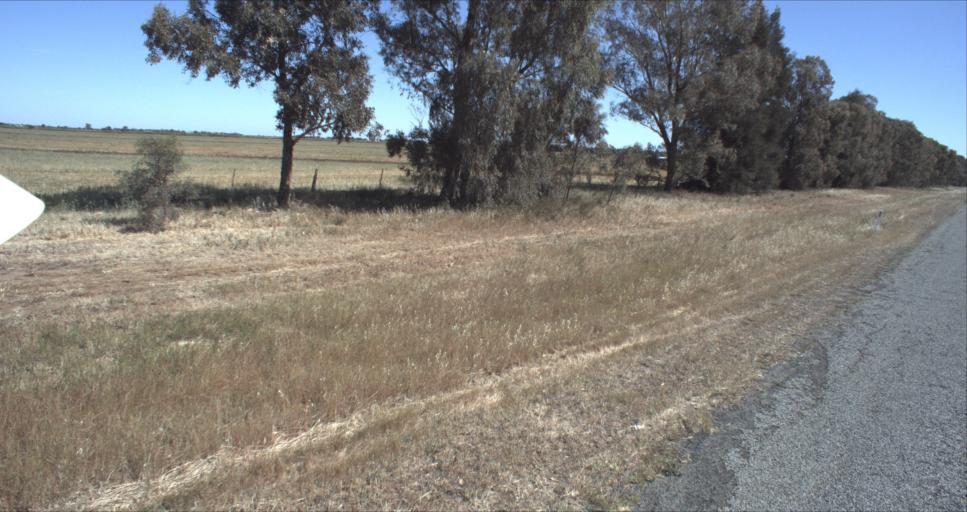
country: AU
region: New South Wales
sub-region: Leeton
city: Leeton
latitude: -34.5372
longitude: 146.3172
